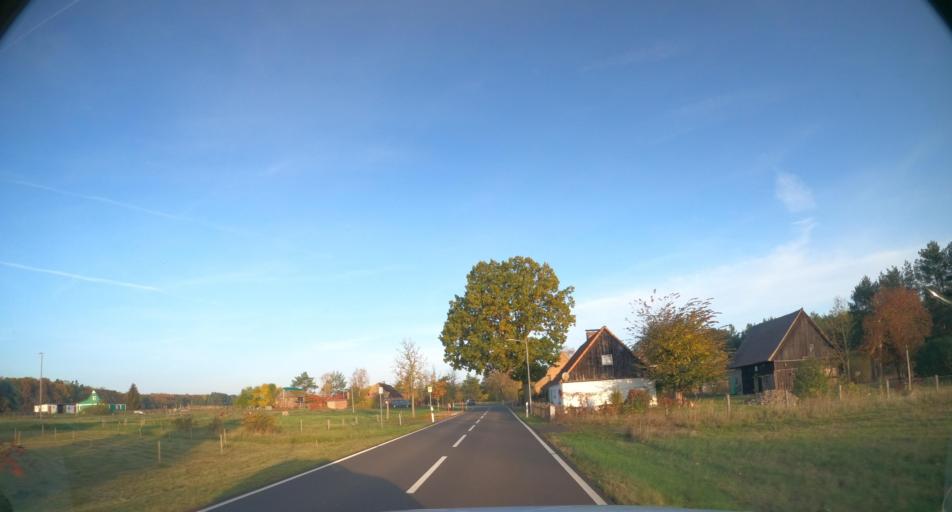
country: DE
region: Mecklenburg-Vorpommern
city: Ahlbeck
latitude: 53.6341
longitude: 14.2230
